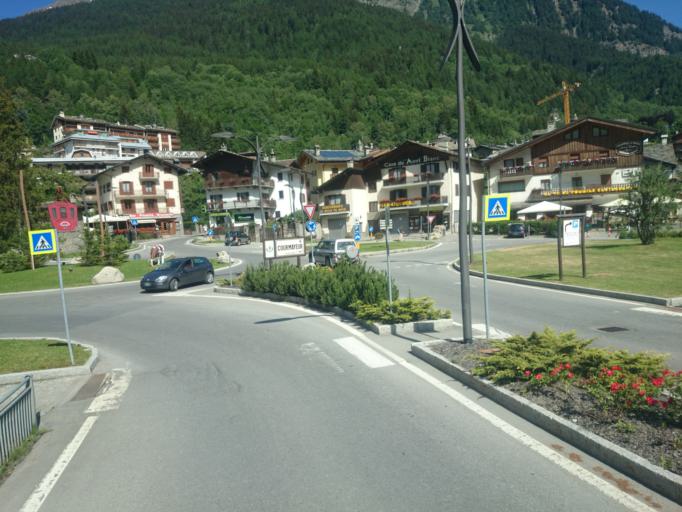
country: IT
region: Aosta Valley
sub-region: Valle d'Aosta
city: Courmayeur
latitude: 45.7908
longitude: 6.9702
